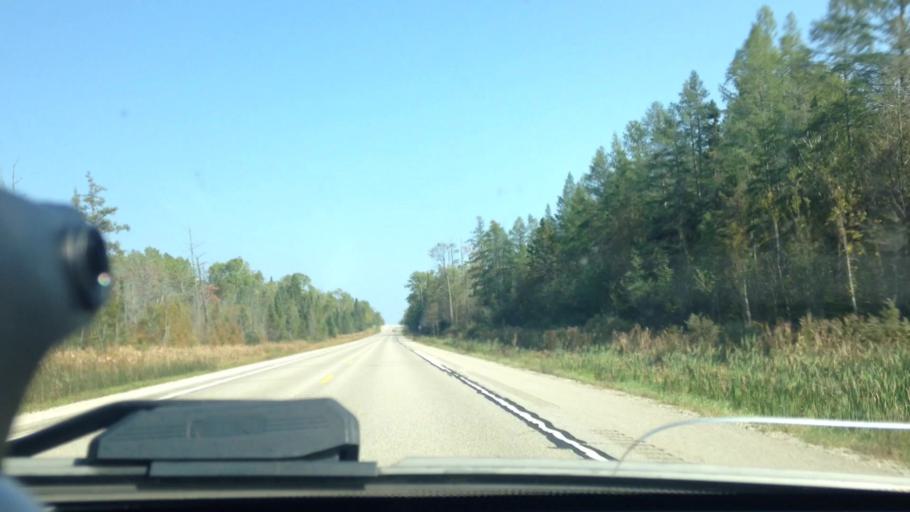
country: US
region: Michigan
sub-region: Luce County
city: Newberry
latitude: 46.3037
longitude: -85.3030
